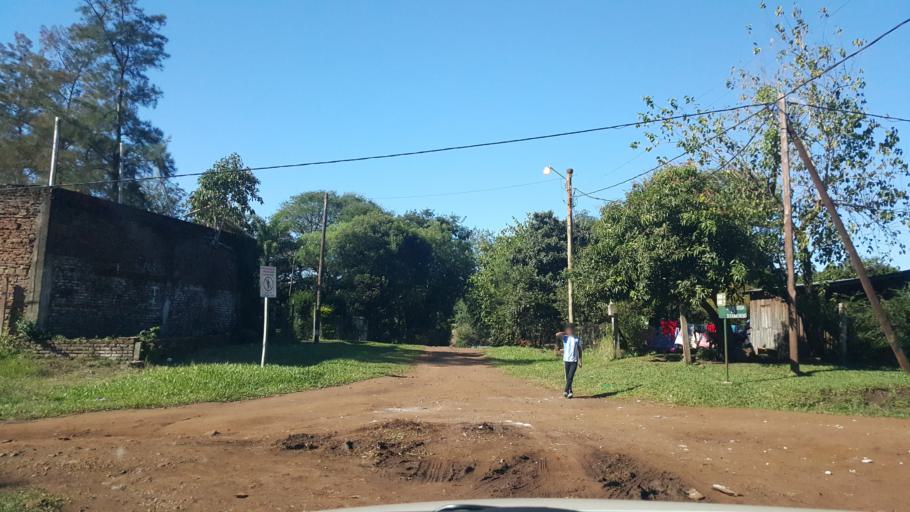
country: AR
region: Misiones
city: Garupa
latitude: -27.4622
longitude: -55.8386
